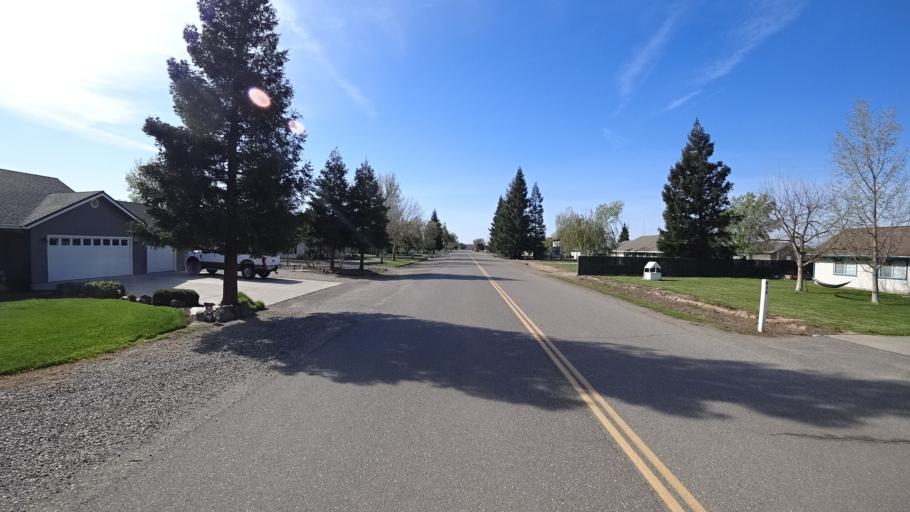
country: US
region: California
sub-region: Glenn County
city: Willows
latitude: 39.6158
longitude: -122.1954
